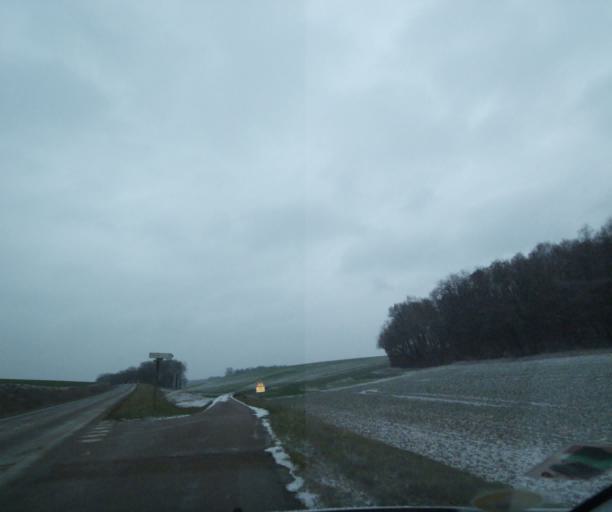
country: FR
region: Champagne-Ardenne
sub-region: Departement de la Haute-Marne
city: Wassy
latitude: 48.4345
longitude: 5.0269
